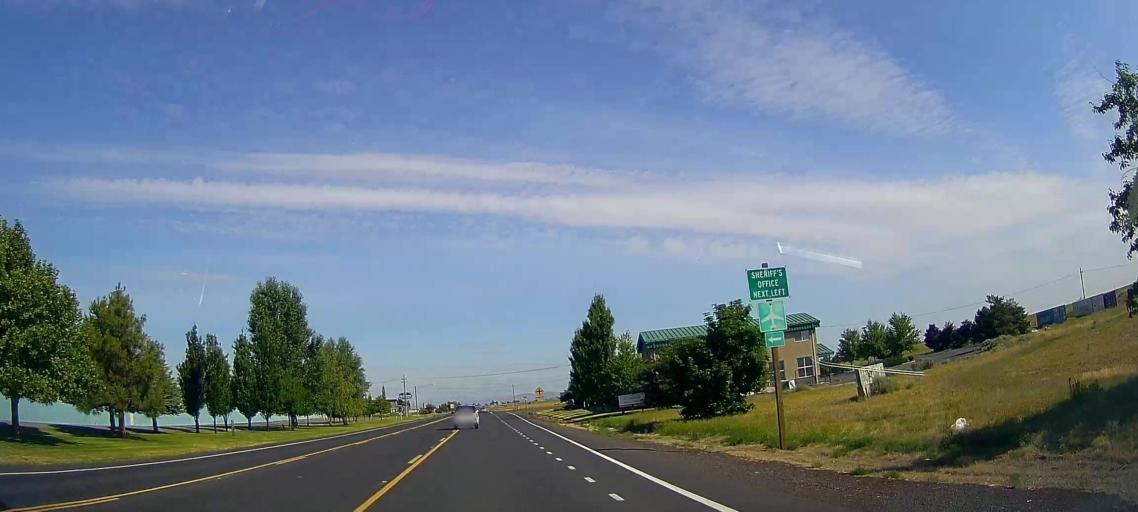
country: US
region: Oregon
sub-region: Jefferson County
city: Madras
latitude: 44.6632
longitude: -121.1348
